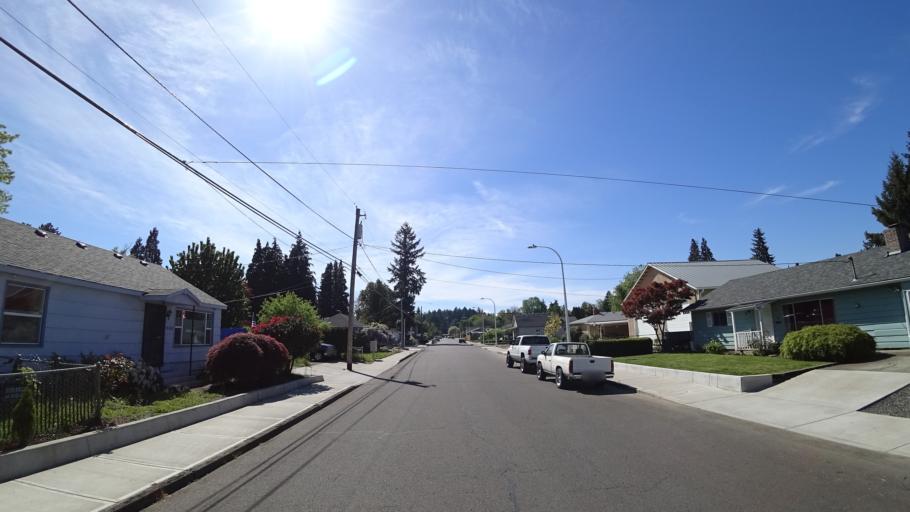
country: US
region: Oregon
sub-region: Washington County
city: Hillsboro
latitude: 45.5135
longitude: -122.9668
